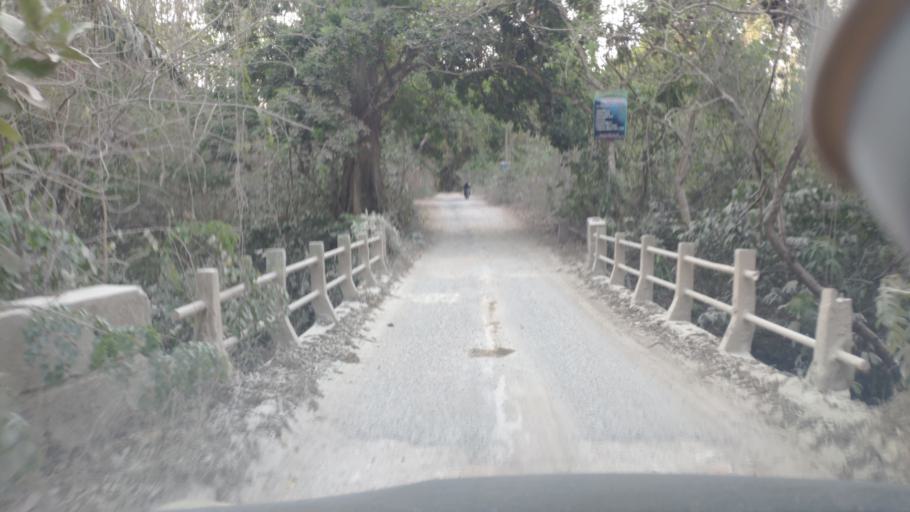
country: ID
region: Central Java
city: Sendangrejo
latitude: -6.9113
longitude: 111.5549
